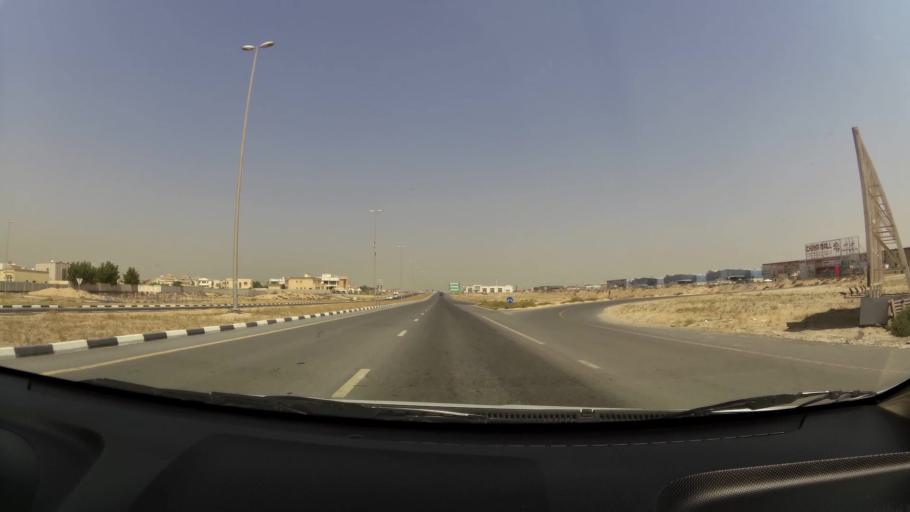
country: AE
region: Ajman
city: Ajman
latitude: 25.4250
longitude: 55.5257
